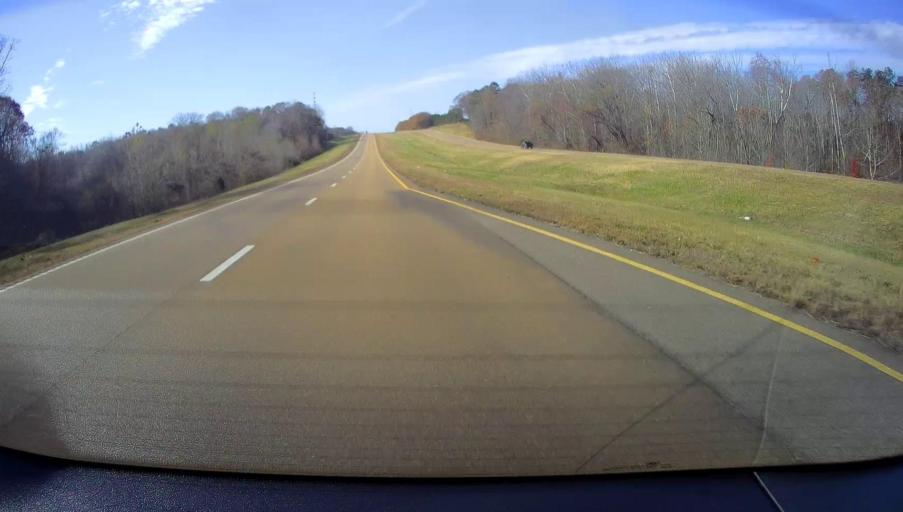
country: US
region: Mississippi
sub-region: Benton County
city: Ashland
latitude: 34.9469
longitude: -89.1263
